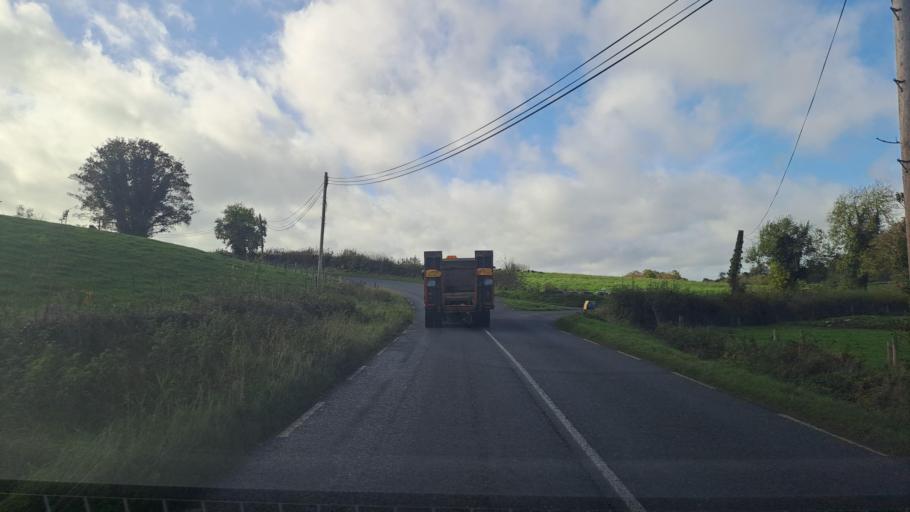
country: IE
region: Ulster
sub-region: County Monaghan
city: Monaghan
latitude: 54.1186
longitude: -6.9223
